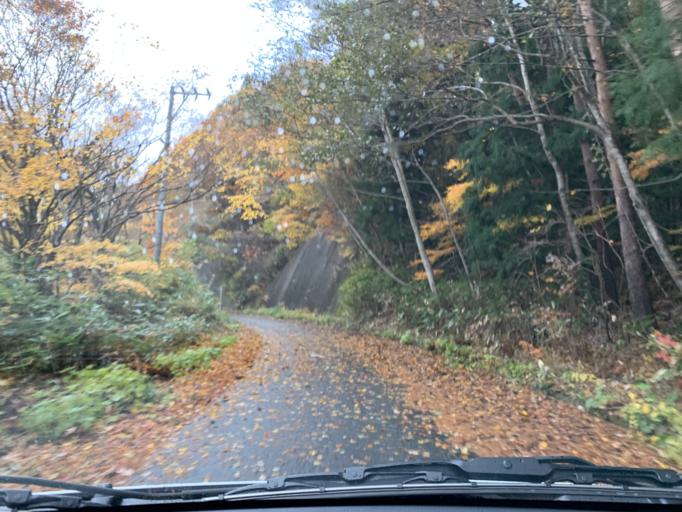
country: JP
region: Iwate
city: Mizusawa
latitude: 39.1018
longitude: 140.9645
